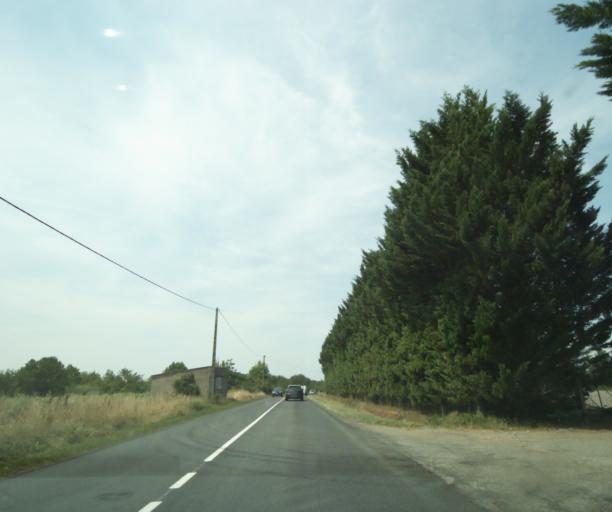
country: FR
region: Poitou-Charentes
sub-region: Departement de la Vienne
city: Chauvigny
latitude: 46.5485
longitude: 0.6406
